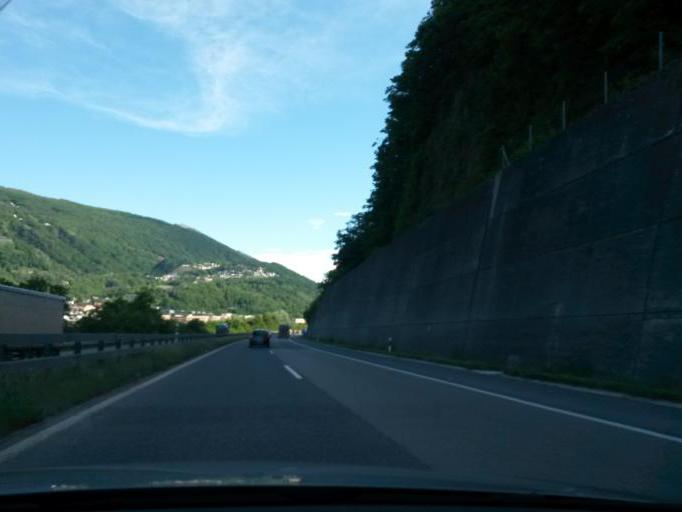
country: CH
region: Ticino
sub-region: Lugano District
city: Agno
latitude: 46.0036
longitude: 8.9153
